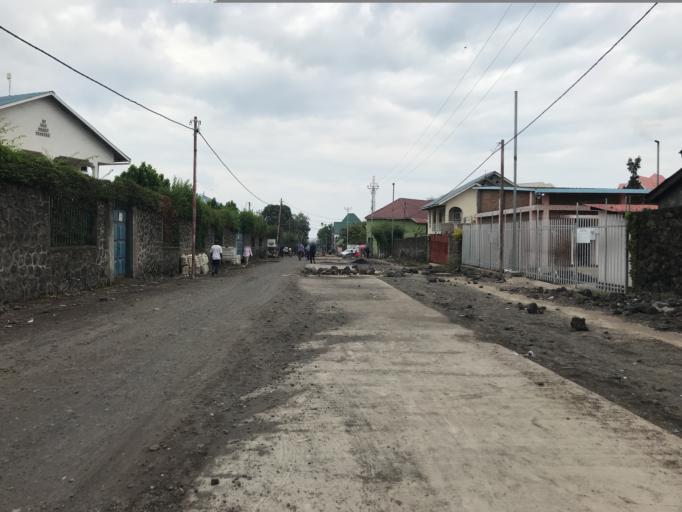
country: CD
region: Nord Kivu
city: Goma
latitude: -1.6857
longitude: 29.2337
